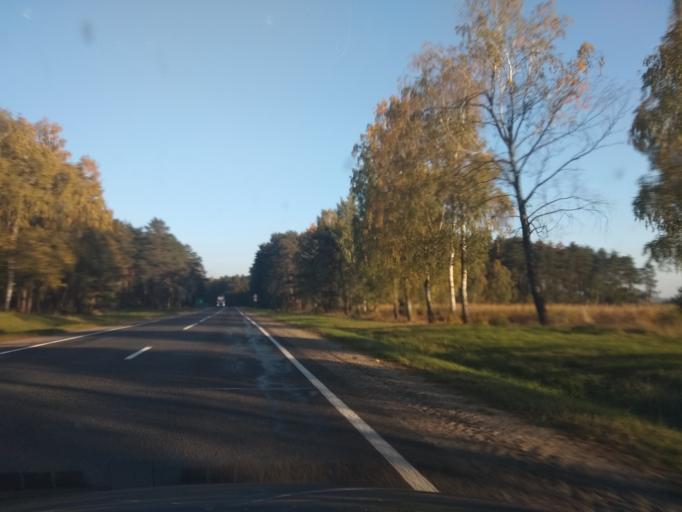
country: BY
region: Grodnenskaya
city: Vawkavysk
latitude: 53.1426
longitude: 24.6233
